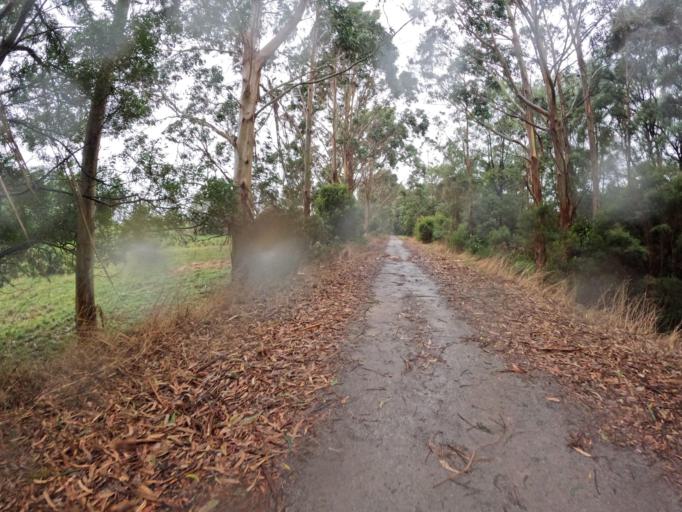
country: AU
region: Victoria
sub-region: Latrobe
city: Morwell
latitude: -38.6910
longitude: 146.1288
